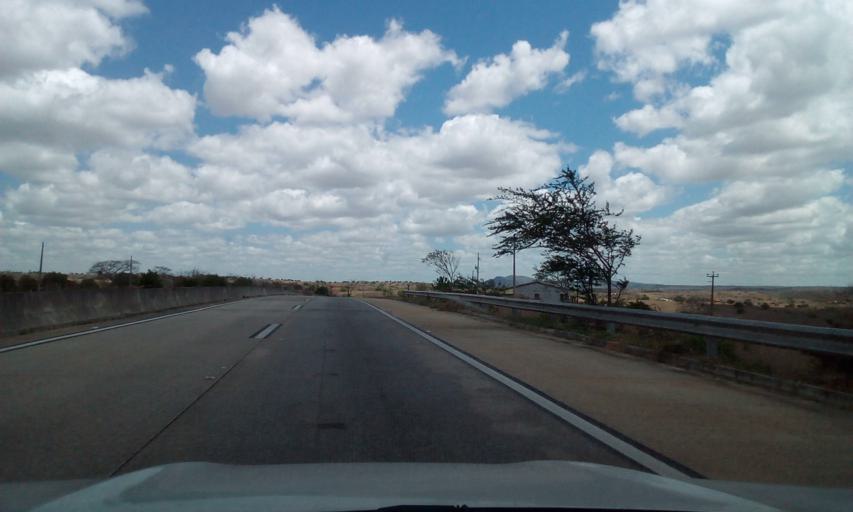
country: BR
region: Alagoas
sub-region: Porto Real Do Colegio
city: Porto Real do Colegio
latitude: -10.1342
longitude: -36.8005
